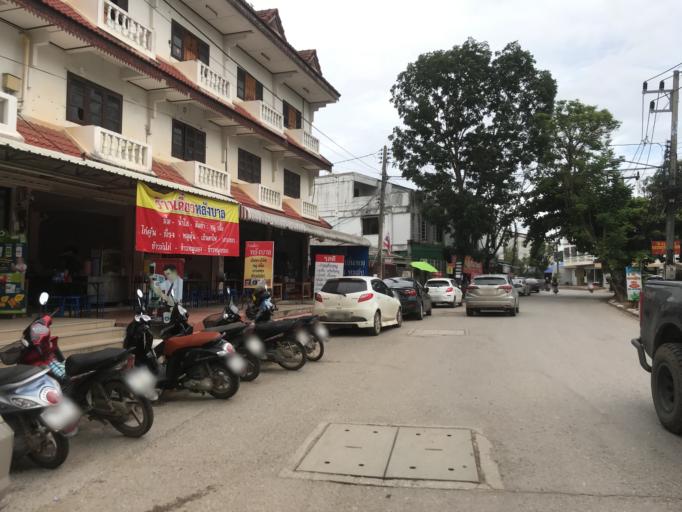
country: TH
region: Chiang Rai
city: Chiang Rai
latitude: 19.8992
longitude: 99.8298
